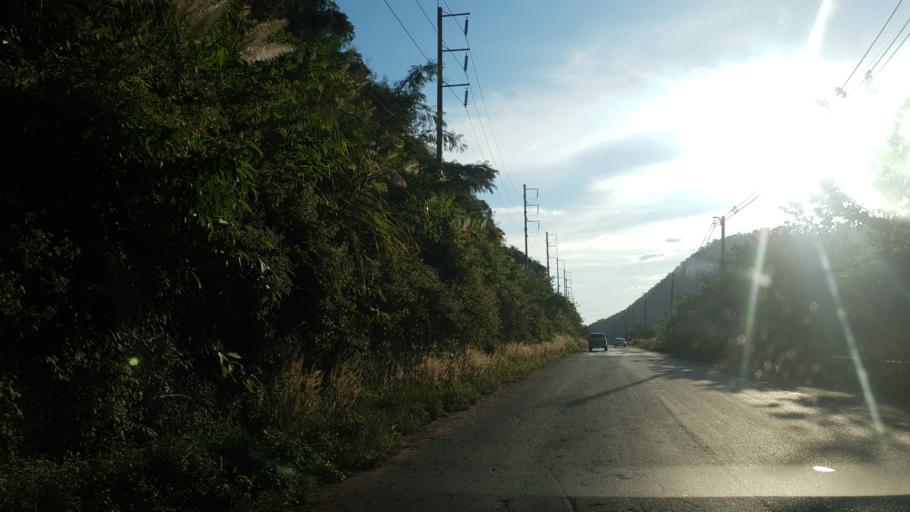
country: TH
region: Loei
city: Dan Sai
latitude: 17.2178
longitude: 101.0233
